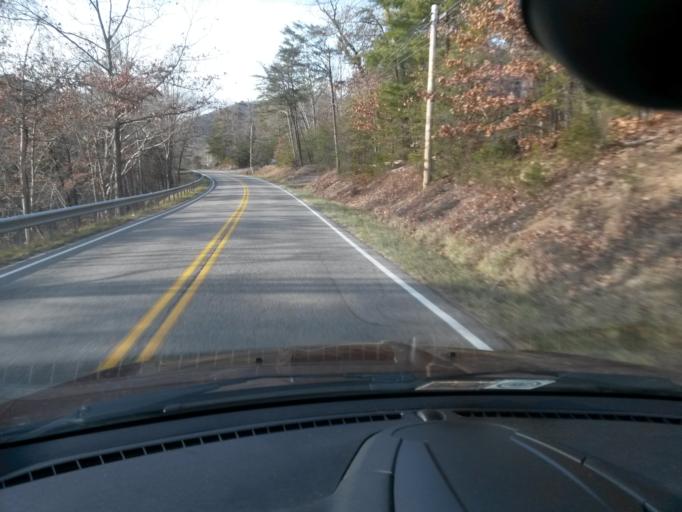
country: US
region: Virginia
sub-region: Rockbridge County
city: East Lexington
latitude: 37.9952
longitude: -79.5080
